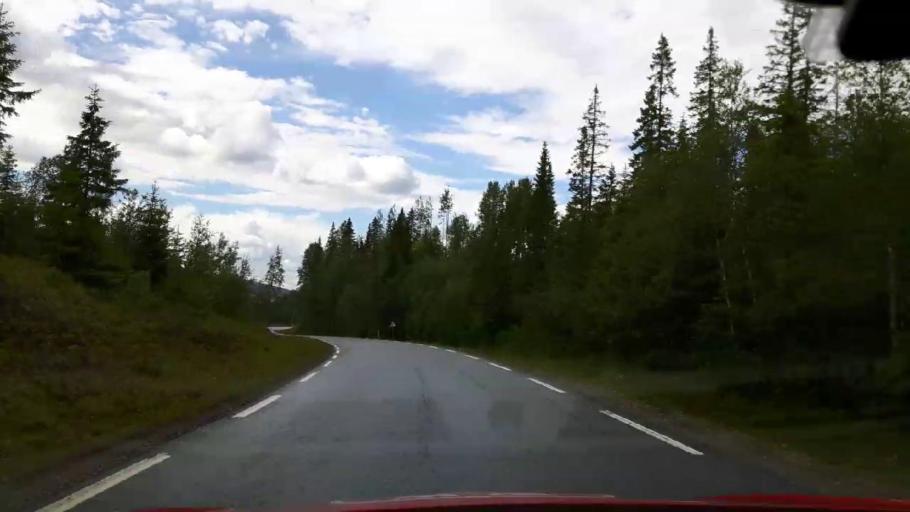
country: NO
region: Nord-Trondelag
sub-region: Lierne
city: Sandvika
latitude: 64.0992
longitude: 14.0300
